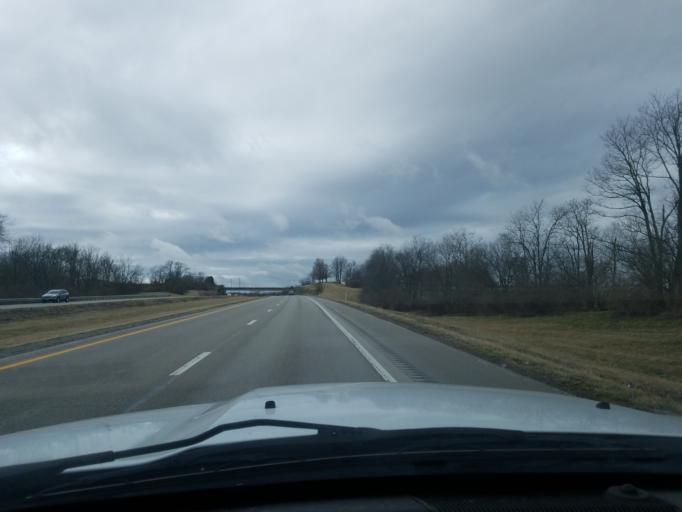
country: US
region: Kentucky
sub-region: Montgomery County
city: Mount Sterling
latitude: 38.0859
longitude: -83.9212
